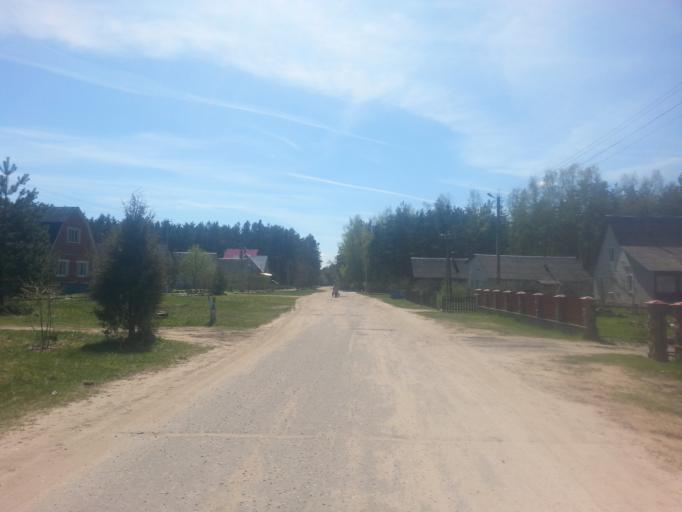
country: BY
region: Minsk
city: Narach
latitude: 54.9276
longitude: 26.6808
